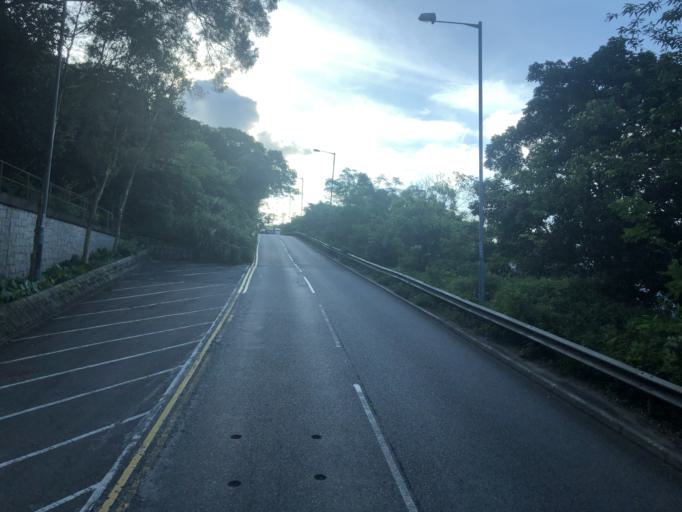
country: HK
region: Sai Kung
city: Sai Kung
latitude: 22.3432
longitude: 114.2551
